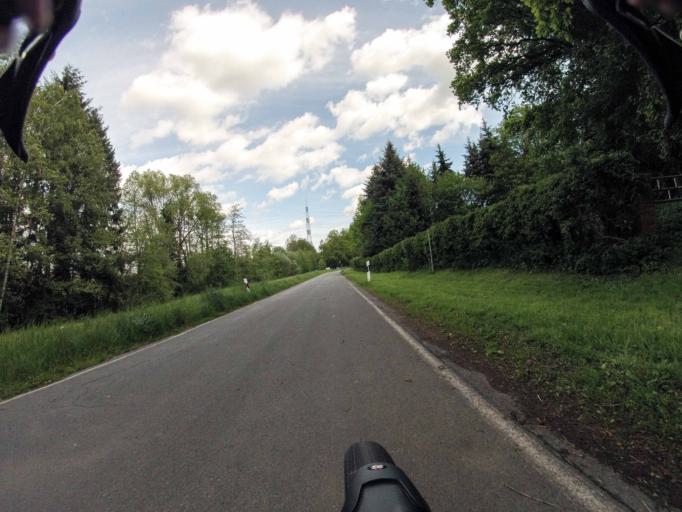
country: DE
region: North Rhine-Westphalia
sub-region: Regierungsbezirk Munster
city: Westerkappeln
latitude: 52.2738
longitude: 7.8533
